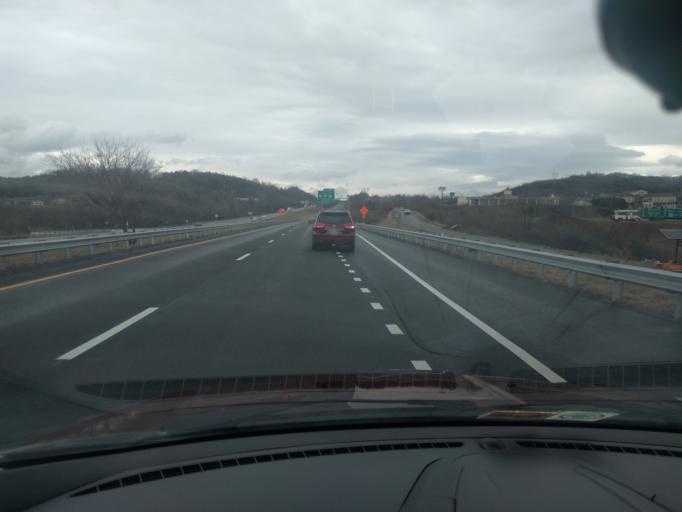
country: US
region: Virginia
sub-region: Botetourt County
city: Daleville
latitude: 37.3887
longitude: -79.9044
